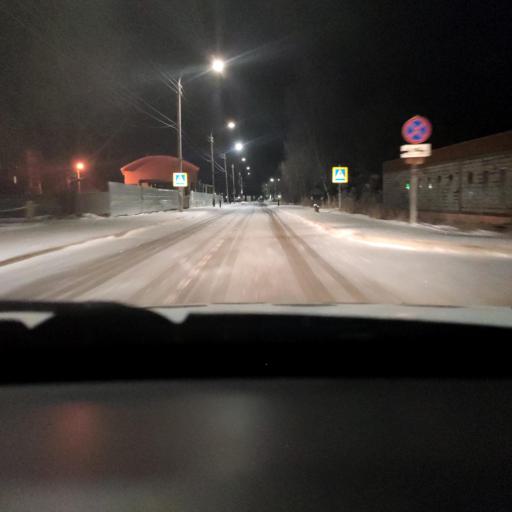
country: RU
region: Perm
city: Ust'-Kachka
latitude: 58.0047
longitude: 55.6726
